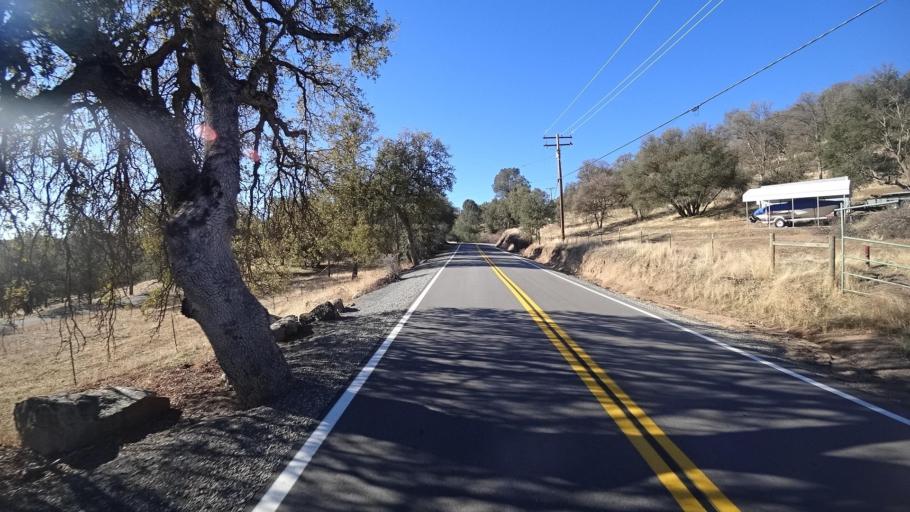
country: US
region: California
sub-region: Kern County
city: Alta Sierra
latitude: 35.7084
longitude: -118.7434
